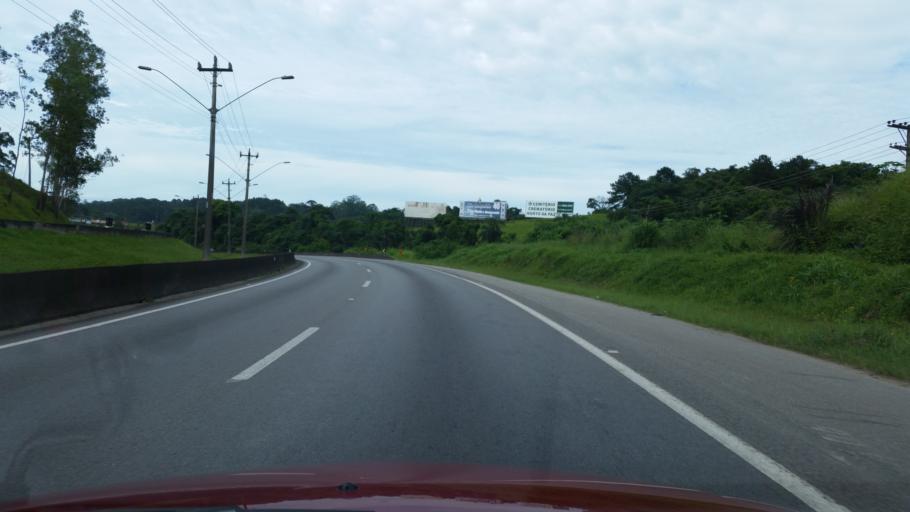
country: BR
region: Sao Paulo
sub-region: Itapecerica Da Serra
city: Itapecerica da Serra
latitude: -23.7231
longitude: -46.8918
